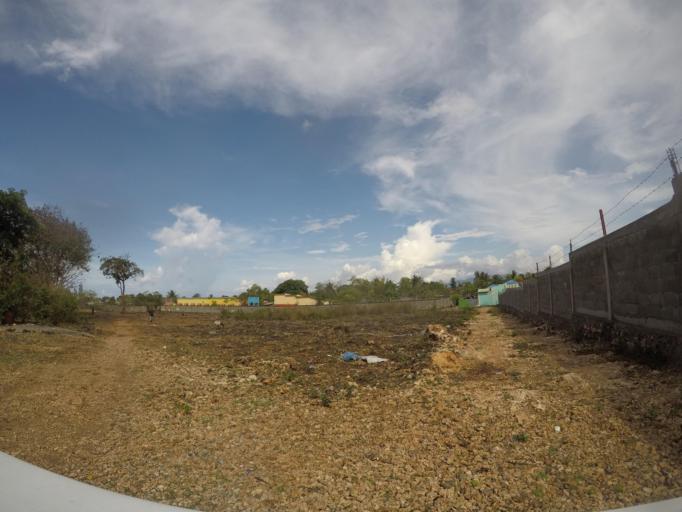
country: TL
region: Baucau
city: Baucau
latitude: -8.4798
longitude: 126.4554
